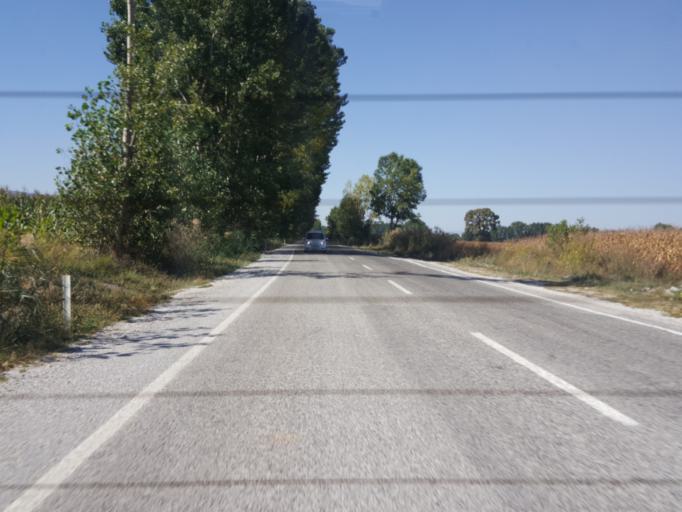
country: TR
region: Tokat
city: Pazar
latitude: 40.2695
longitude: 36.2252
